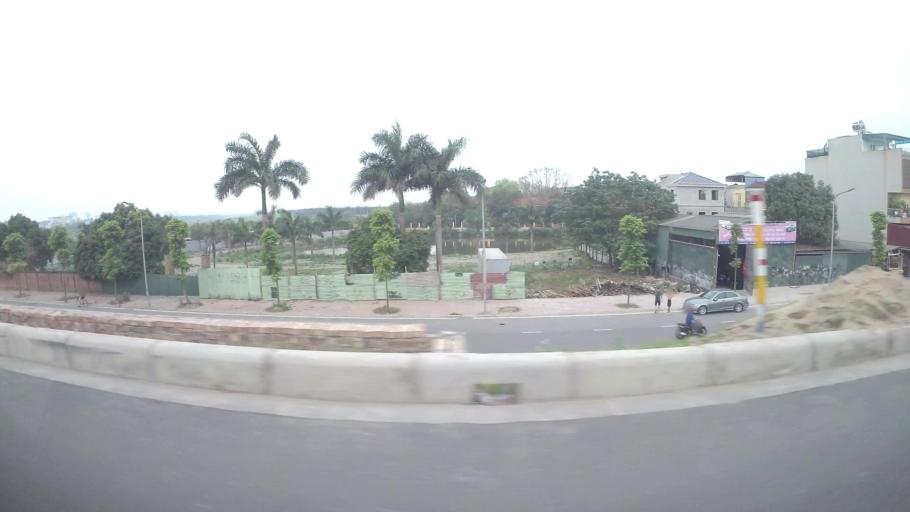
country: VN
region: Ha Noi
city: Hoan Kiem
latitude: 21.0288
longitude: 105.8814
